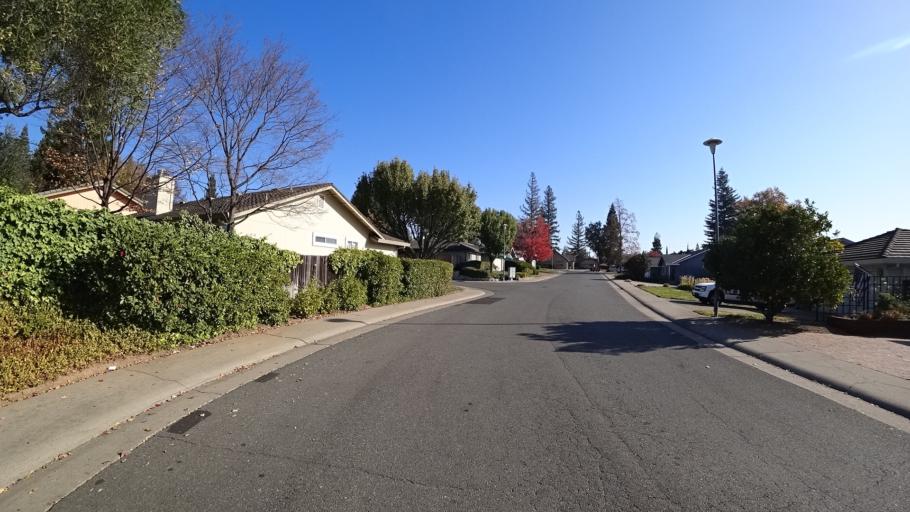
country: US
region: California
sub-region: Sacramento County
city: Citrus Heights
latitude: 38.6847
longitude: -121.2843
